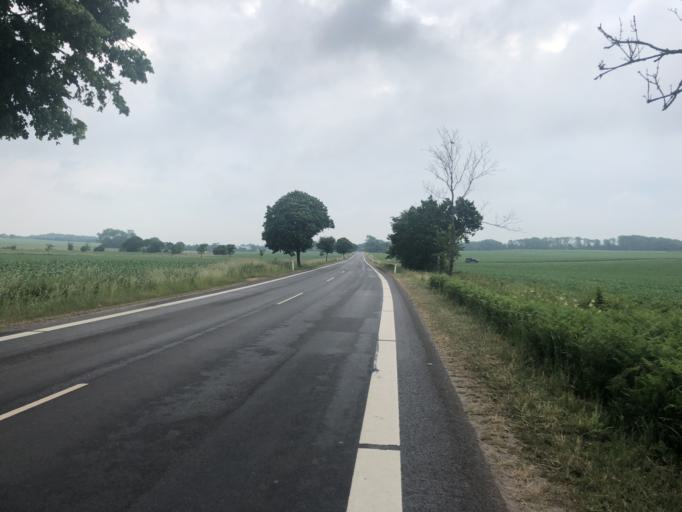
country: DK
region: Capital Region
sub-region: Bornholm Kommune
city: Akirkeby
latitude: 55.1520
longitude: 14.9053
